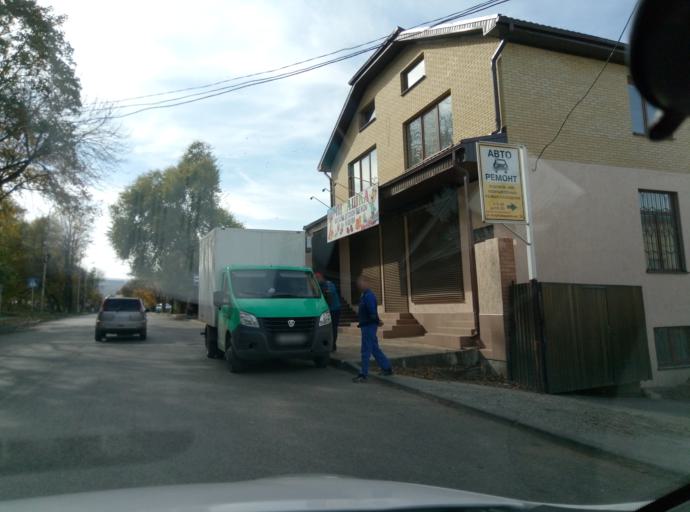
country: RU
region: Stavropol'skiy
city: Kislovodsk
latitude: 43.9218
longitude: 42.7037
